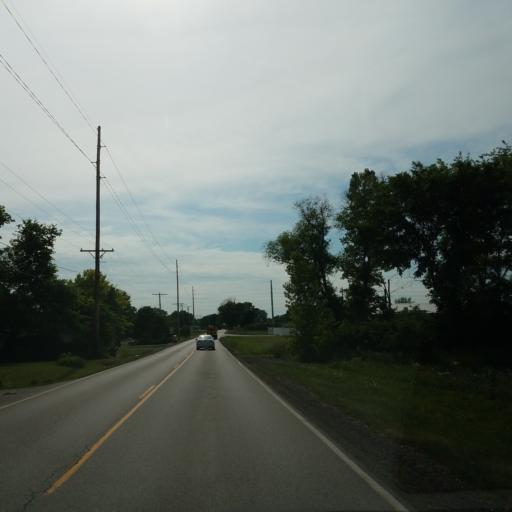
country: US
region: Illinois
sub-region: McLean County
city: Bloomington
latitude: 40.4514
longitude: -88.9768
